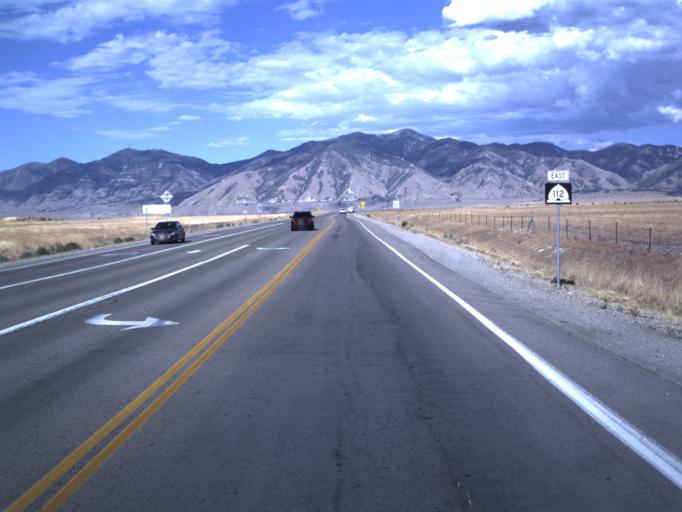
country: US
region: Utah
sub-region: Tooele County
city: Tooele
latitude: 40.5484
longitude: -112.3417
